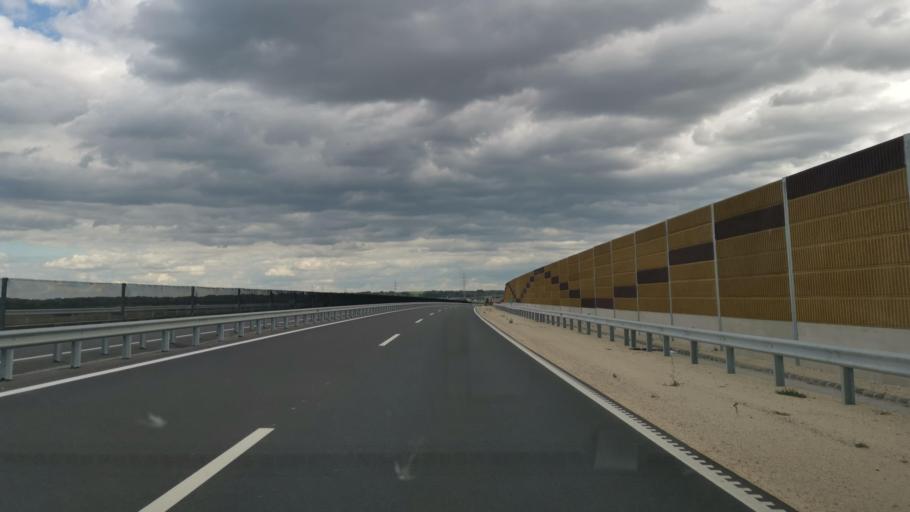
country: HU
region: Jasz-Nagykun-Szolnok
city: Szajol
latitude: 47.2173
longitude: 20.2583
